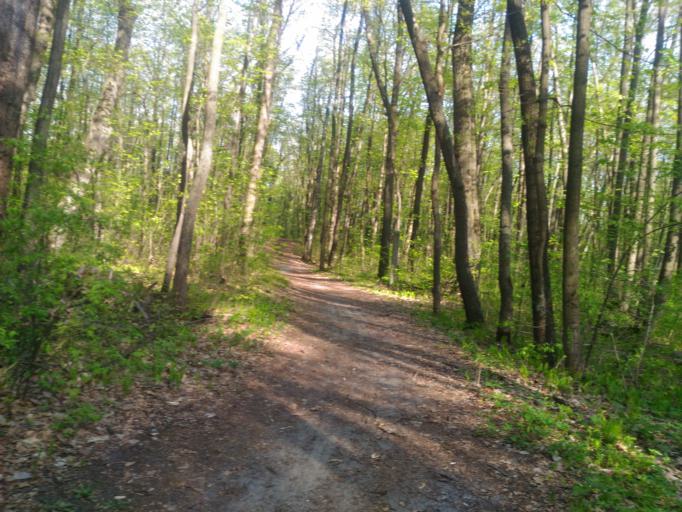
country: RU
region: Ulyanovsk
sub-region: Ulyanovskiy Rayon
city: Ulyanovsk
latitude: 54.2708
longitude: 48.3429
